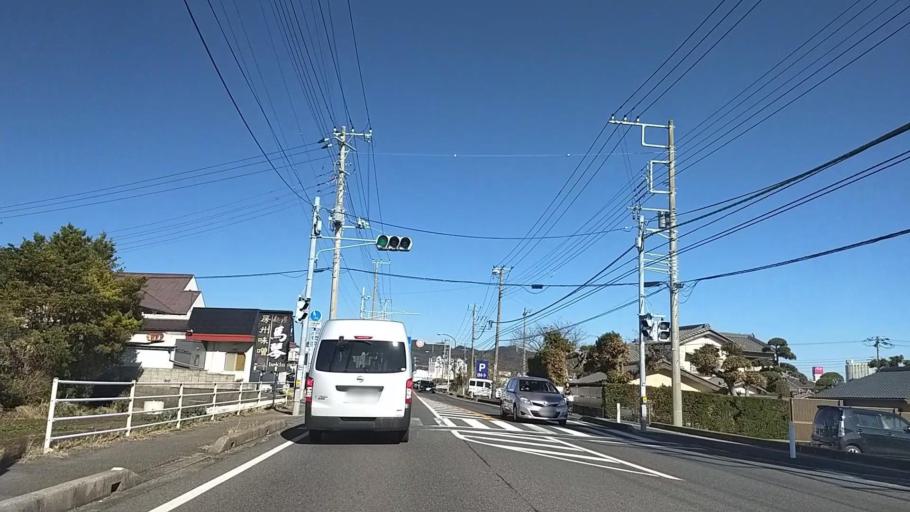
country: JP
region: Chiba
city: Kawaguchi
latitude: 35.1042
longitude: 140.0959
